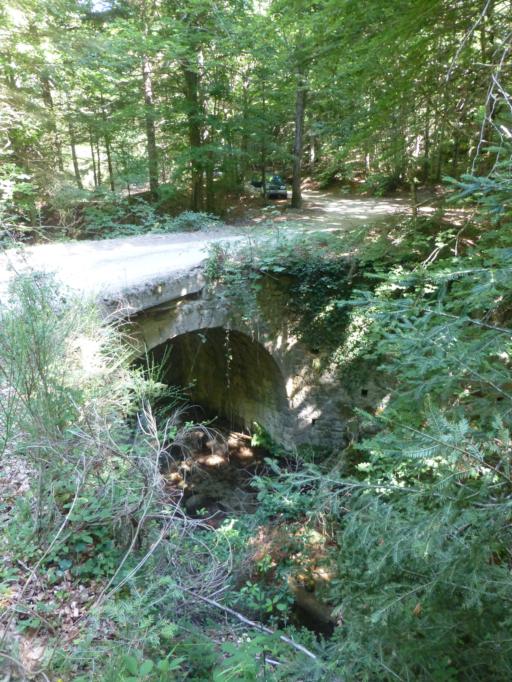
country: IT
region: Calabria
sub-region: Provincia di Vibo-Valentia
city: Nardodipace
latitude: 38.5226
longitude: 16.3812
